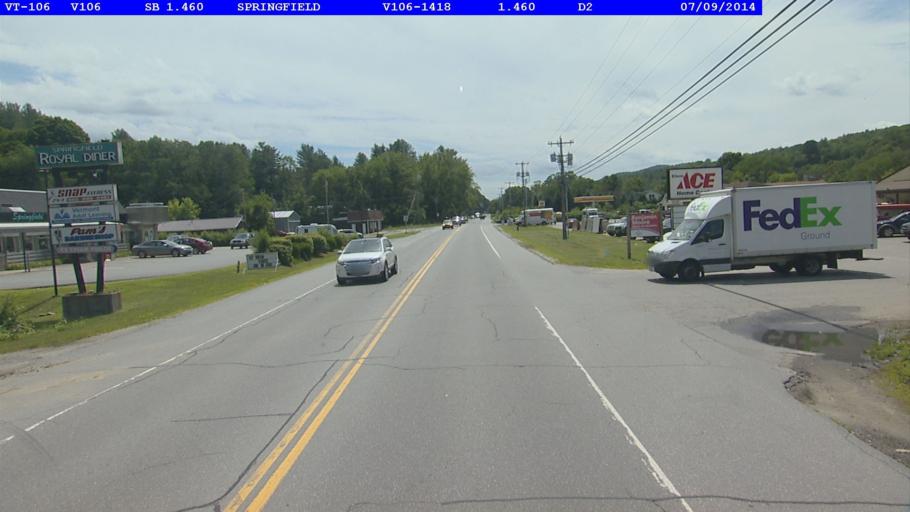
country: US
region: Vermont
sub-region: Windsor County
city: Springfield
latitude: 43.3216
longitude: -72.5070
